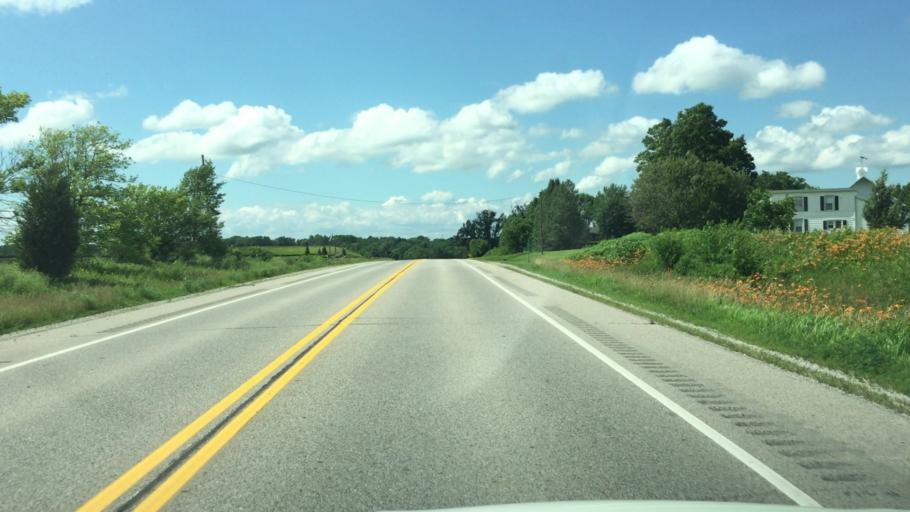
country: US
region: Iowa
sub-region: Johnson County
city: Solon
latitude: 41.7623
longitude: -91.4799
